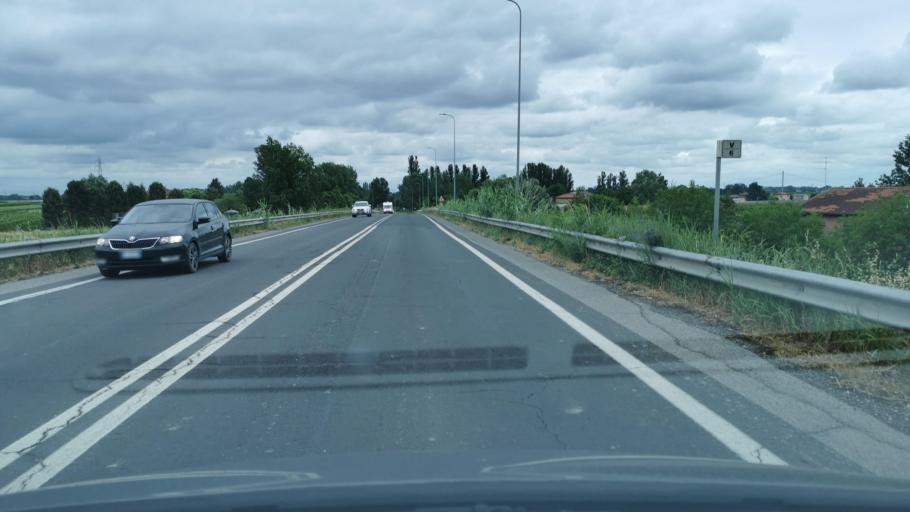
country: IT
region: Emilia-Romagna
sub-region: Provincia di Ravenna
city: Granarolo
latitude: 44.3690
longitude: 11.9397
